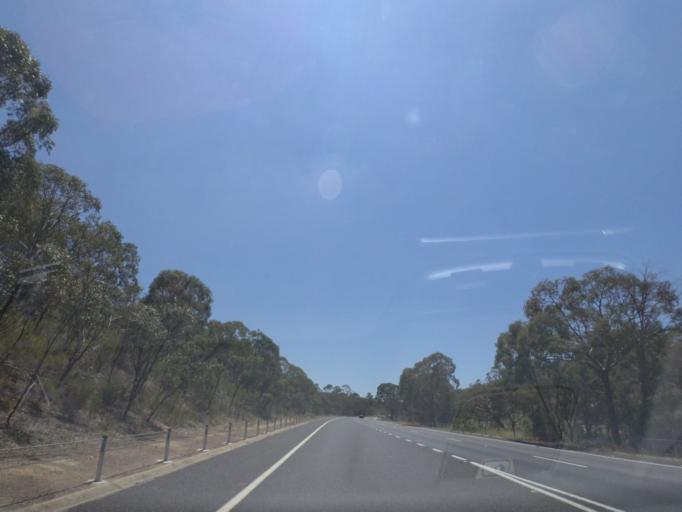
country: AU
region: Victoria
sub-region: Murrindindi
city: Kinglake West
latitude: -36.9612
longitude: 145.1839
